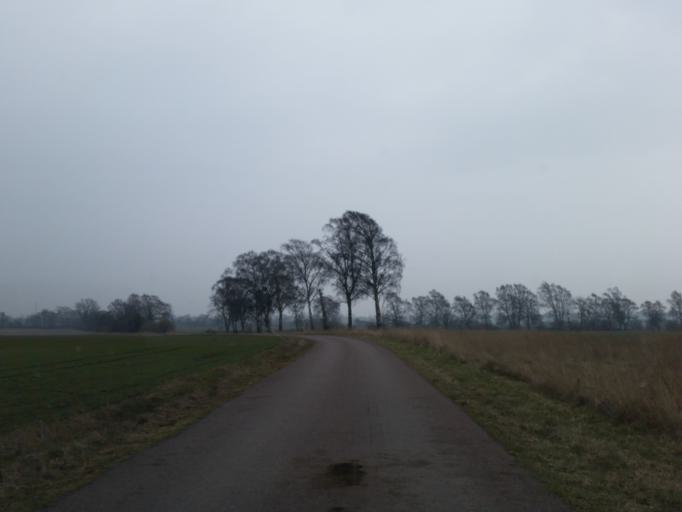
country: SE
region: Kalmar
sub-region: Morbylanga Kommun
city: Moerbylanga
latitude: 56.4520
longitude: 16.4020
